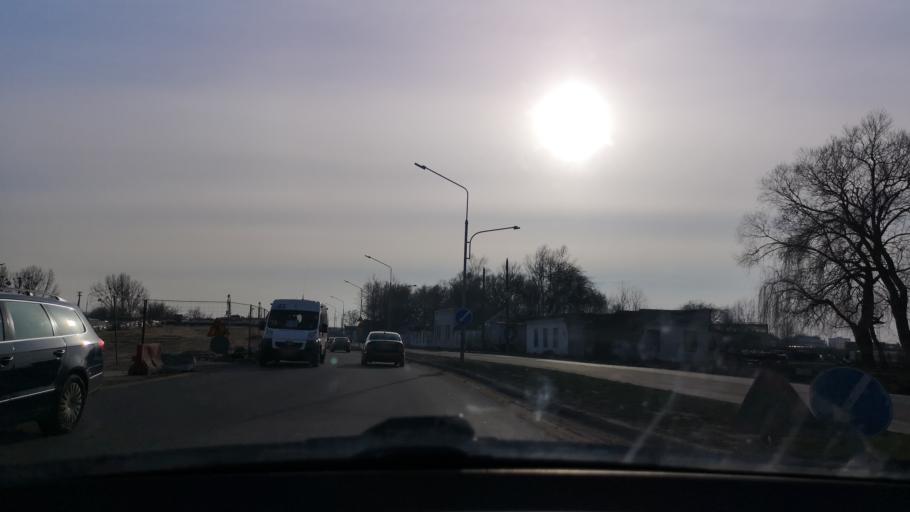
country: BY
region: Brest
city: Brest
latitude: 52.1107
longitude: 23.6674
